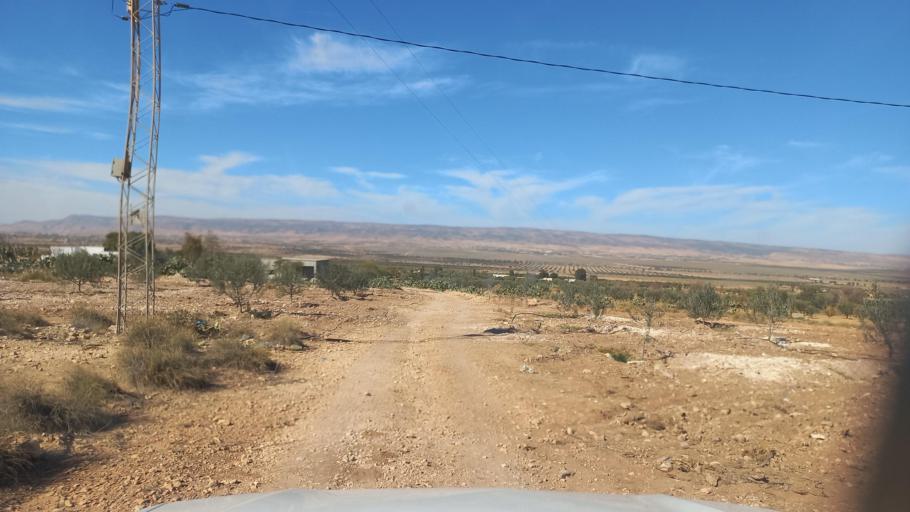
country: TN
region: Al Qasrayn
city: Kasserine
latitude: 35.2008
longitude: 8.9720
